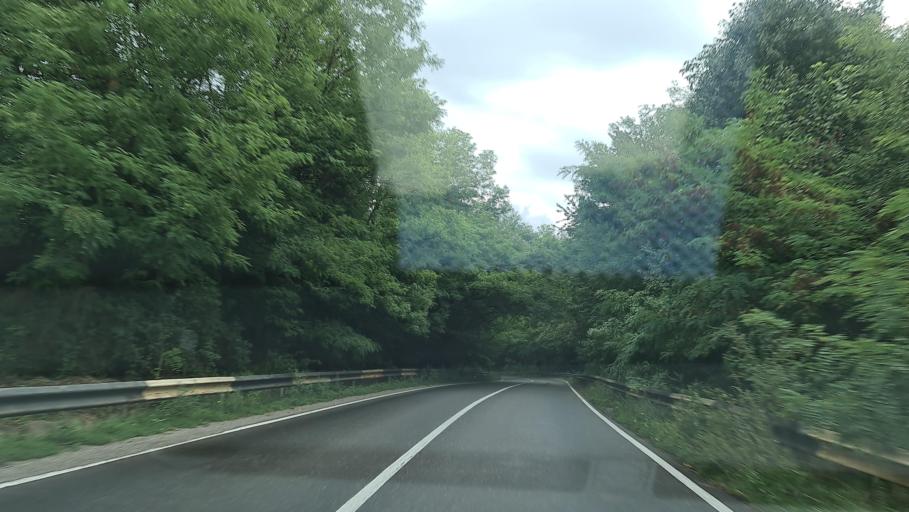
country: RO
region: Neamt
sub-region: Comuna Borlesti
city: Borlesti
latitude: 46.7705
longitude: 26.4859
